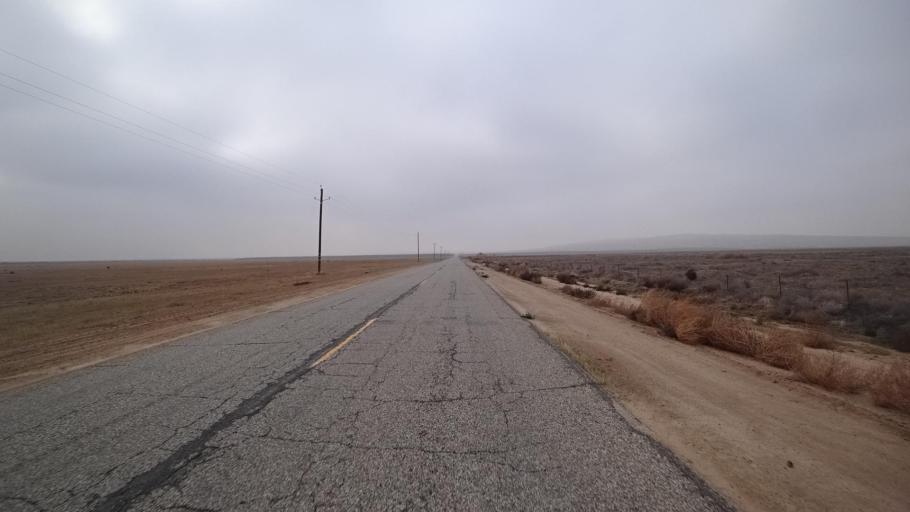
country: US
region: California
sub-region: Kern County
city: Maricopa
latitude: 35.1230
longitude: -119.3279
